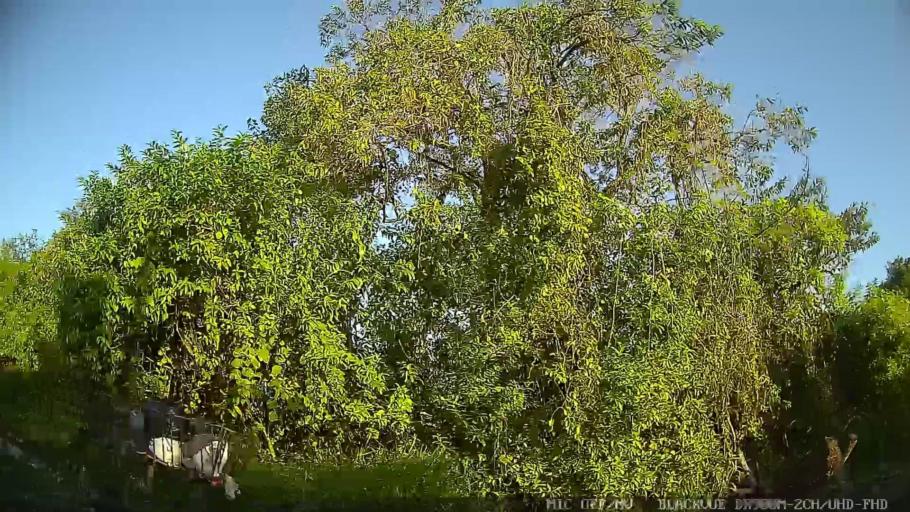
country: BR
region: Sao Paulo
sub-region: Guaruja
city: Guaruja
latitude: -23.9724
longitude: -46.2717
